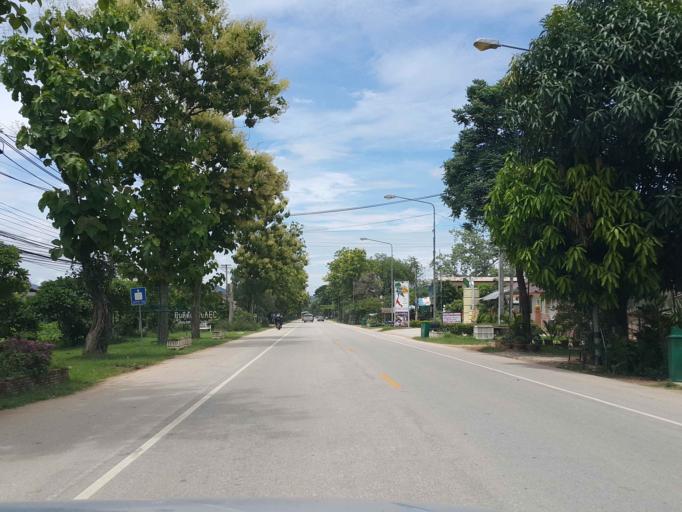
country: TH
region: Sukhothai
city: Ban Na
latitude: 17.0175
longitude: 99.7228
